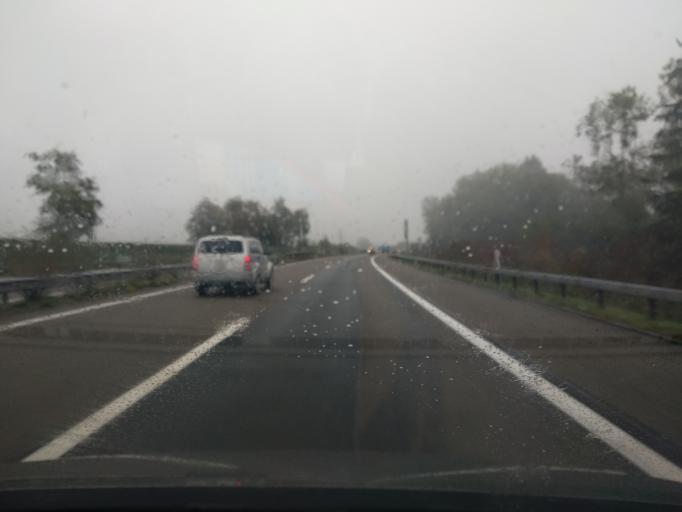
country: CH
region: Saint Gallen
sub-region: Wahlkreis Wil
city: Zuzwil
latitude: 47.4620
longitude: 9.1061
